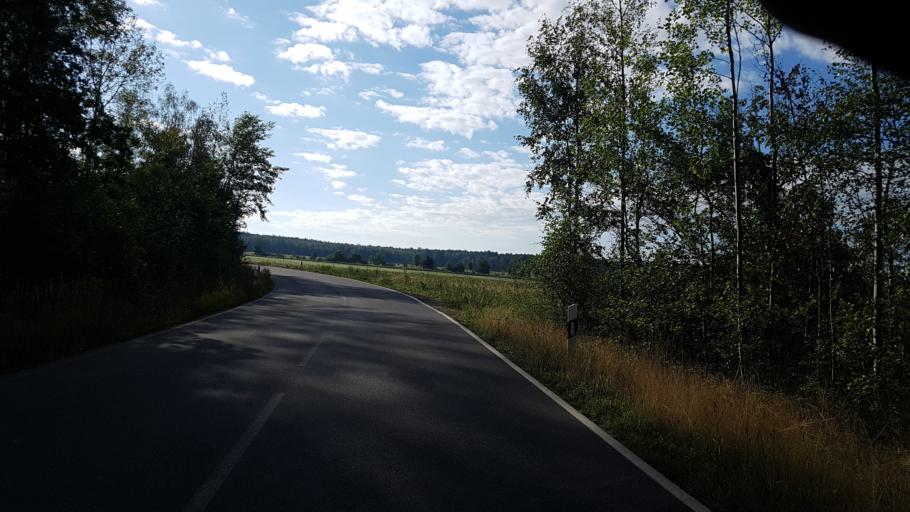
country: DE
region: Brandenburg
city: Welzow
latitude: 51.5347
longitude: 14.2441
